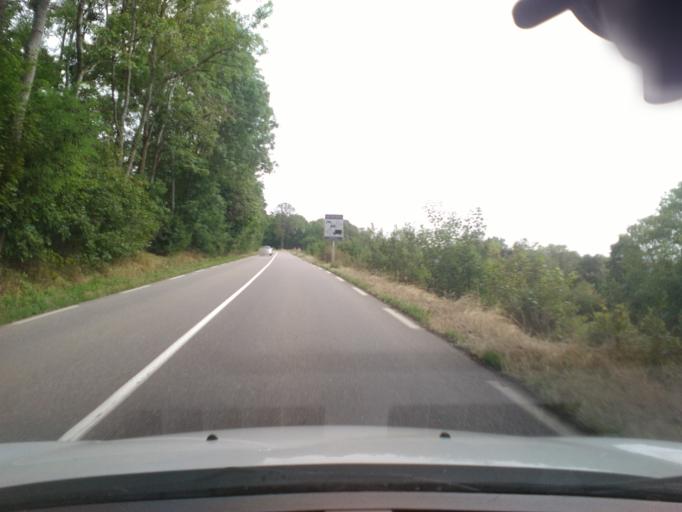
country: FR
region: Lorraine
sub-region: Departement de Meurthe-et-Moselle
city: Pulligny
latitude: 48.5278
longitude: 6.1727
